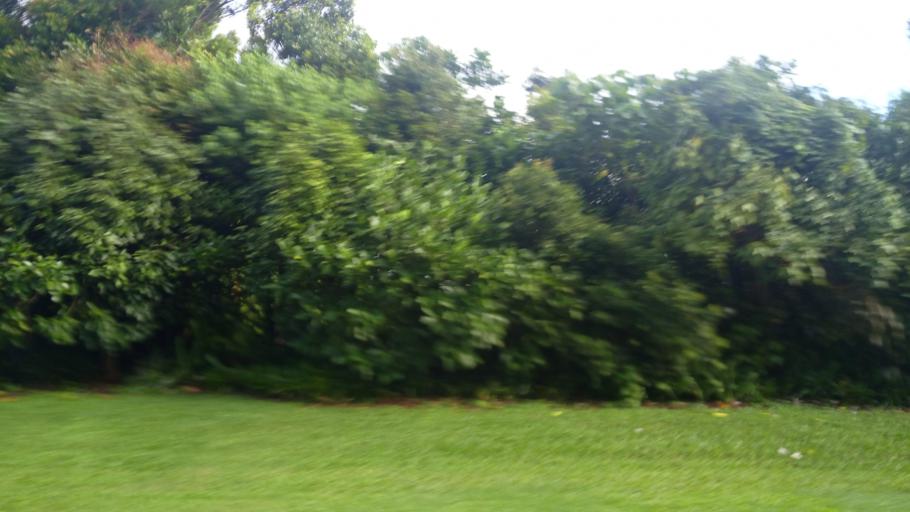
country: AU
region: Queensland
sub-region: Cassowary Coast
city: Innisfail
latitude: -17.5389
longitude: 145.9645
